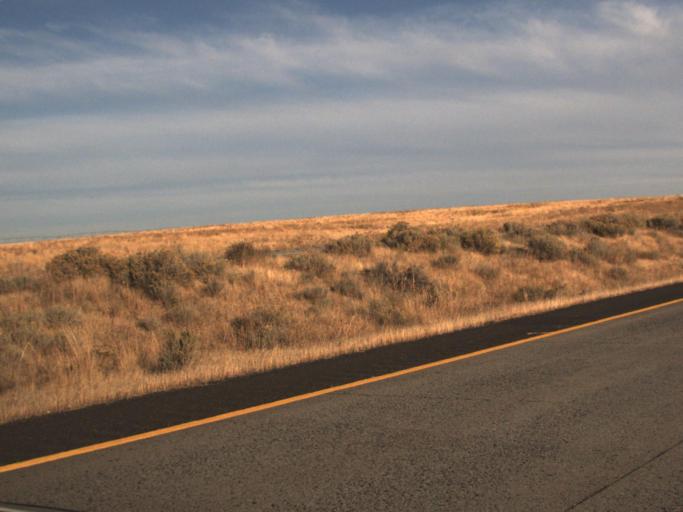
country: US
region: Washington
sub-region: Franklin County
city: Connell
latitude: 46.7067
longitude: -118.8361
